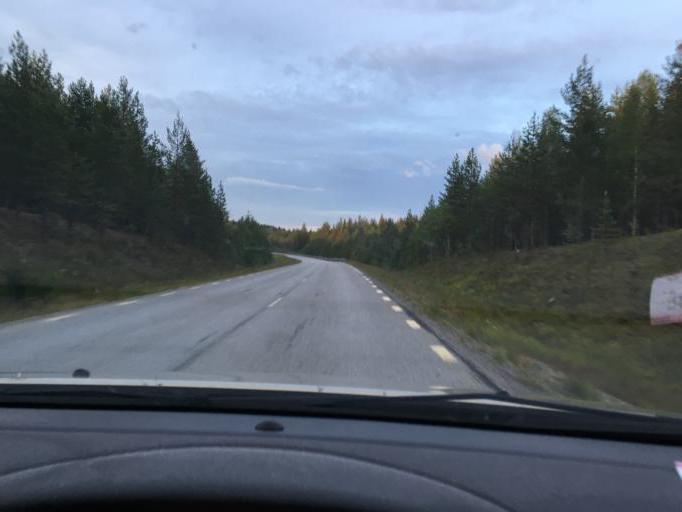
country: SE
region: Norrbotten
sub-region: Lulea Kommun
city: Ranea
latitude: 66.0484
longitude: 22.2611
